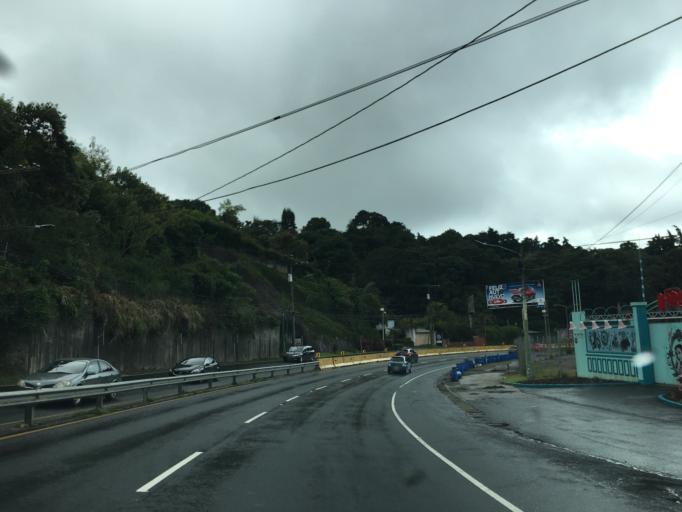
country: GT
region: Guatemala
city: Santa Catarina Pinula
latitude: 14.5785
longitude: -90.4843
